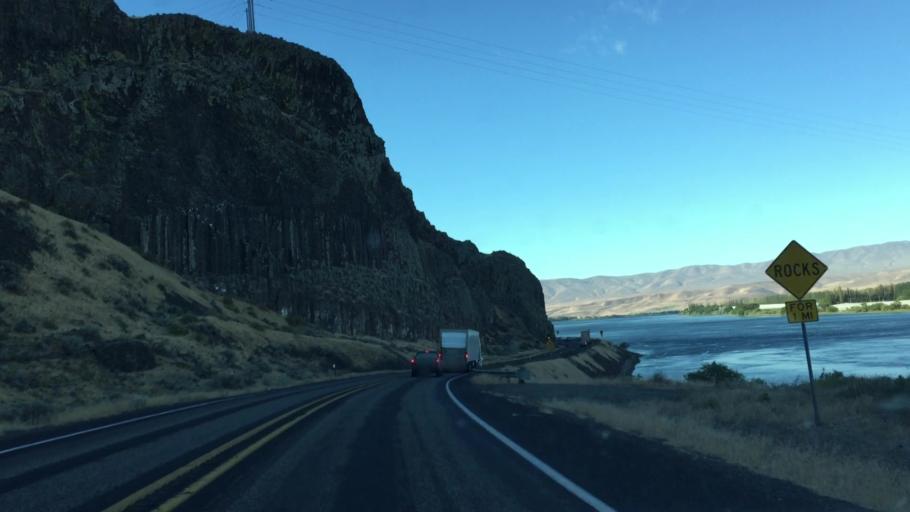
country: US
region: Washington
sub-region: Grant County
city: Mattawa
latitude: 46.8020
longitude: -119.9232
